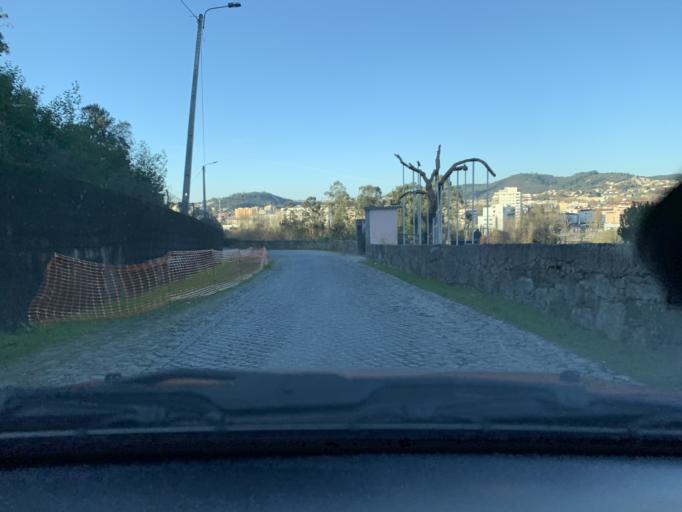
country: PT
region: Braga
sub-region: Vila Nova de Famalicao
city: Vila Nova de Famalicao
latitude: 41.4076
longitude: -8.5088
